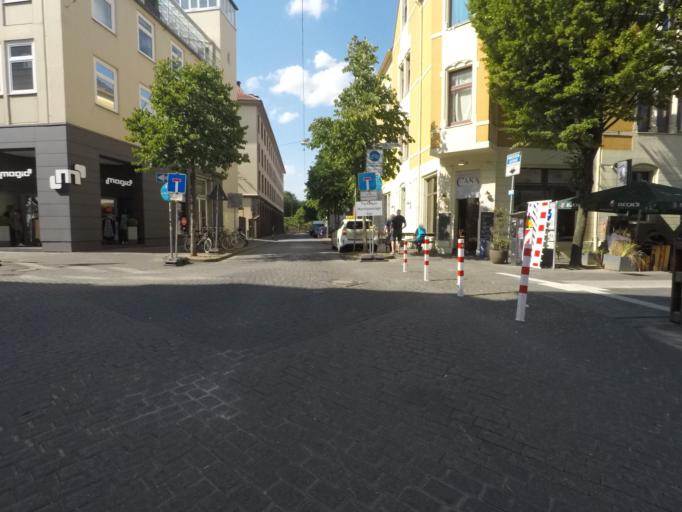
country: DE
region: North Rhine-Westphalia
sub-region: Regierungsbezirk Detmold
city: Bielefeld
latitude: 52.0252
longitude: 8.5301
